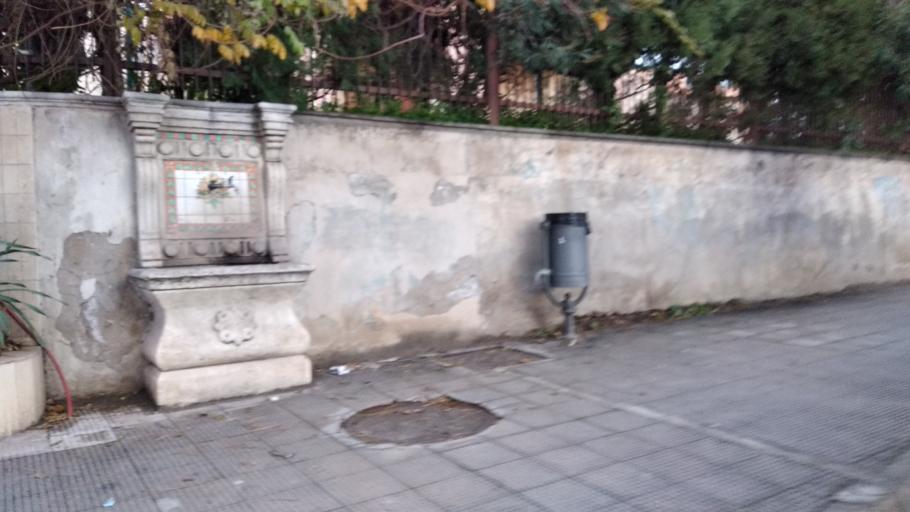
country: IT
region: Calabria
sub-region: Provincia di Catanzaro
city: Roccelletta
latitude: 38.8276
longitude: 16.6217
